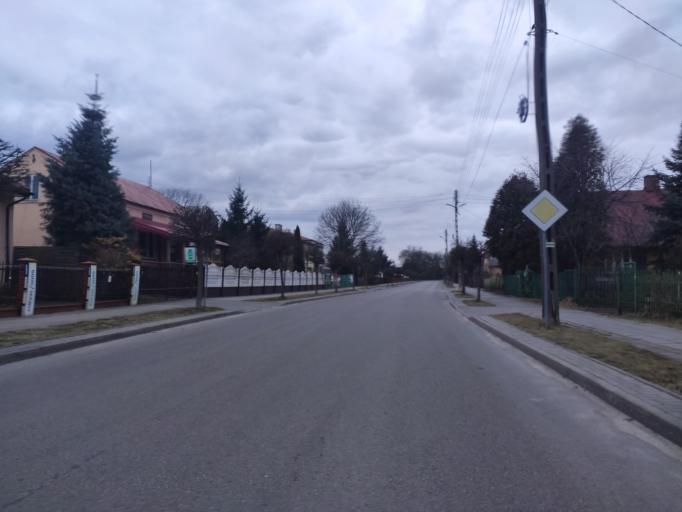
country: PL
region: Lublin Voivodeship
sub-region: Powiat lubartowski
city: Kock
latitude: 51.6416
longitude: 22.4407
